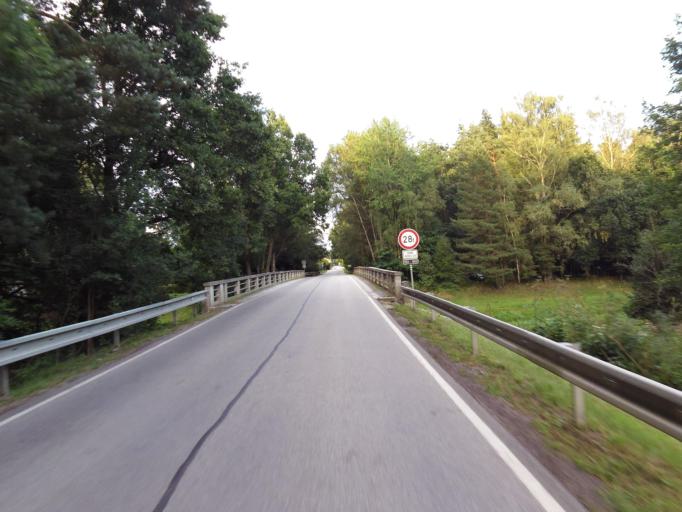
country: CZ
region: Jihocesky
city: Chlum u Trebone
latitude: 48.9487
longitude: 14.8804
